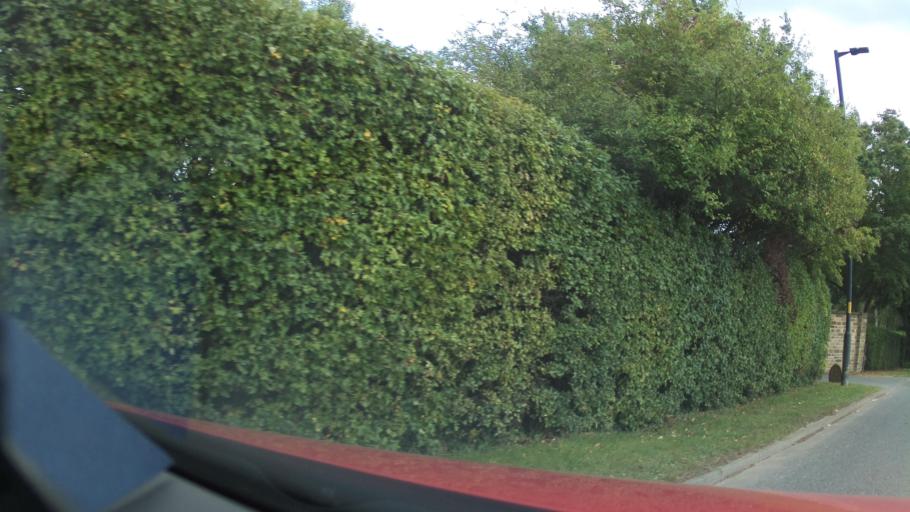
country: GB
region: England
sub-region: North Yorkshire
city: Ripon
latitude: 54.1485
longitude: -1.5308
